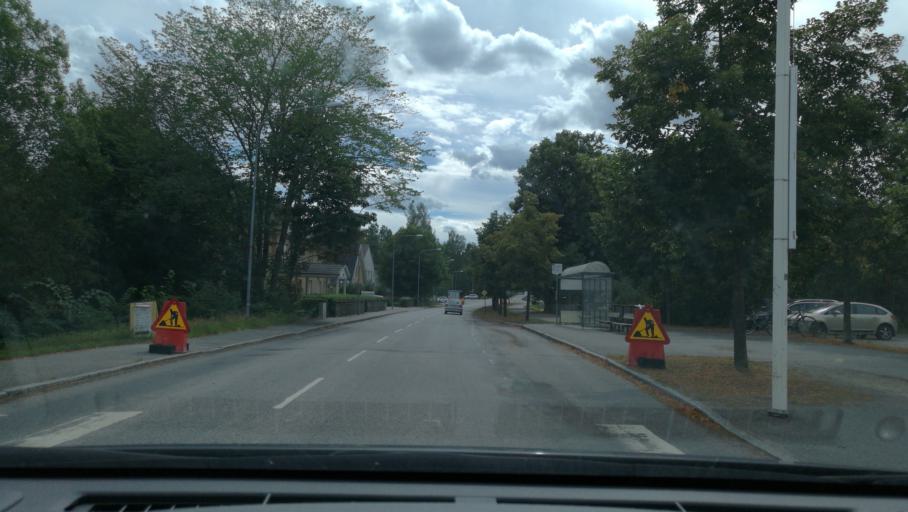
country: SE
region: OEstergoetland
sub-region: Norrkopings Kommun
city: Jursla
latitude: 58.6644
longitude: 16.1811
